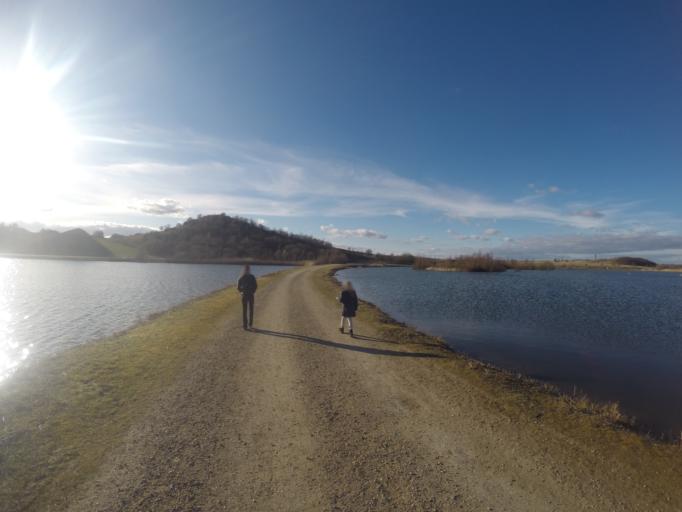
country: DK
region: Zealand
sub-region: Greve Kommune
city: Tune
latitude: 55.6250
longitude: 12.1784
